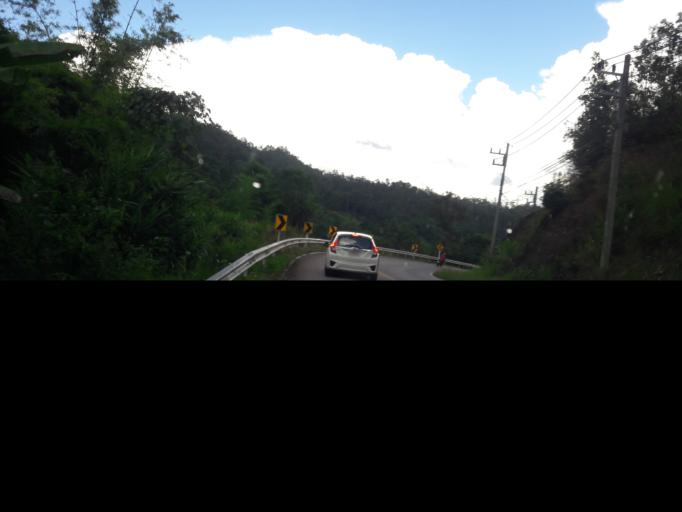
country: TH
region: Mae Hong Son
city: Wiang Nuea
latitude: 19.4406
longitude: 98.3503
